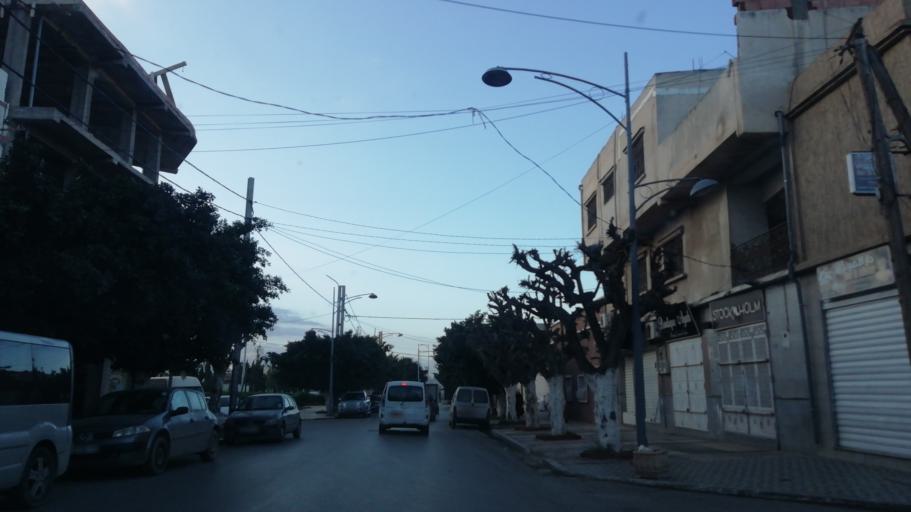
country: DZ
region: Oran
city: Oran
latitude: 35.6796
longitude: -0.6564
